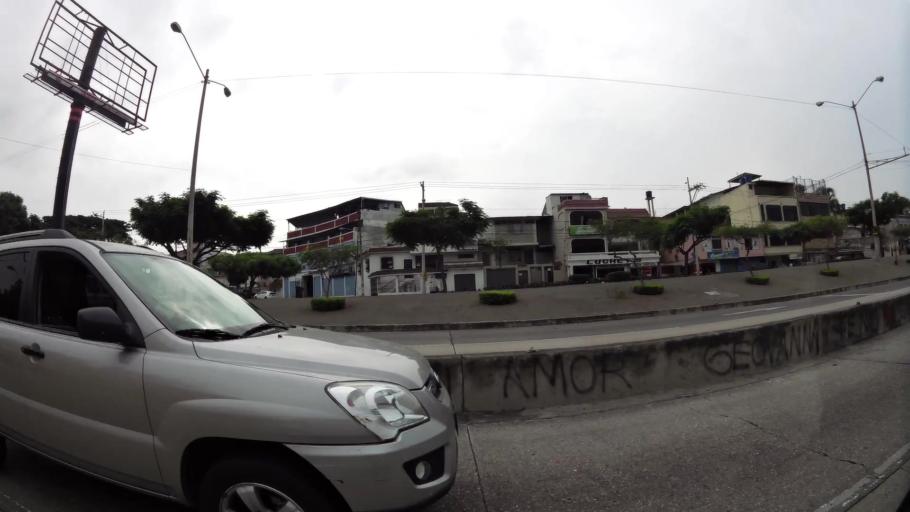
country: EC
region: Guayas
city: Eloy Alfaro
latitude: -2.1338
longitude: -79.8955
